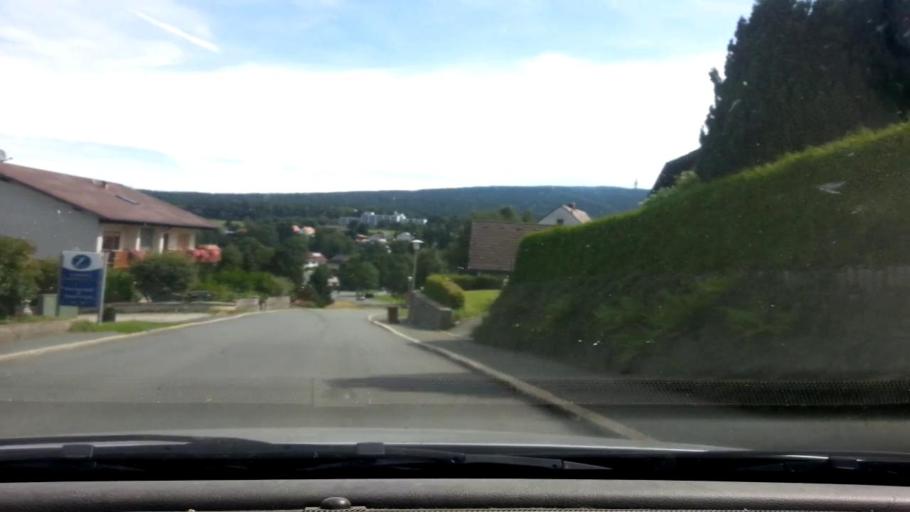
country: DE
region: Bavaria
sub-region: Upper Franconia
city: Bischofsgrun
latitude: 50.0515
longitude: 11.8060
